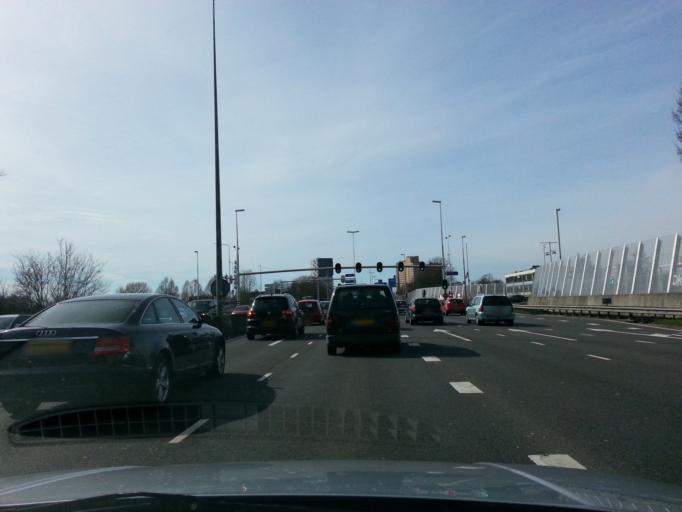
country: NL
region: Groningen
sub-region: Gemeente Groningen
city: Groningen
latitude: 53.2036
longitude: 6.5662
